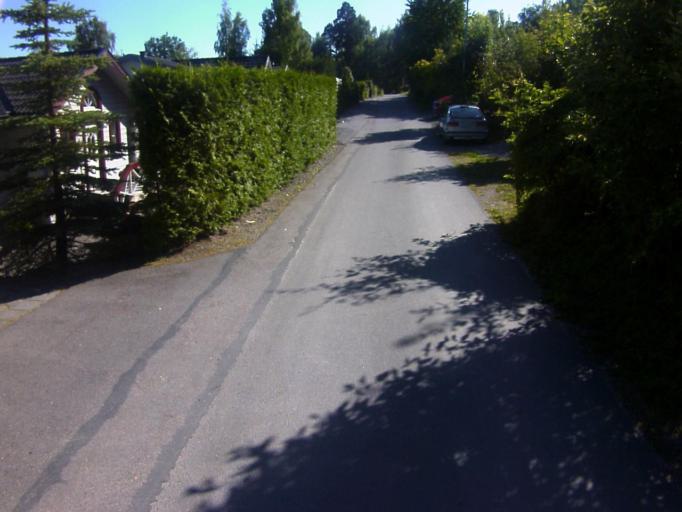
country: SE
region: Soedermanland
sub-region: Eskilstuna Kommun
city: Hallbybrunn
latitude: 59.3374
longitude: 16.4234
